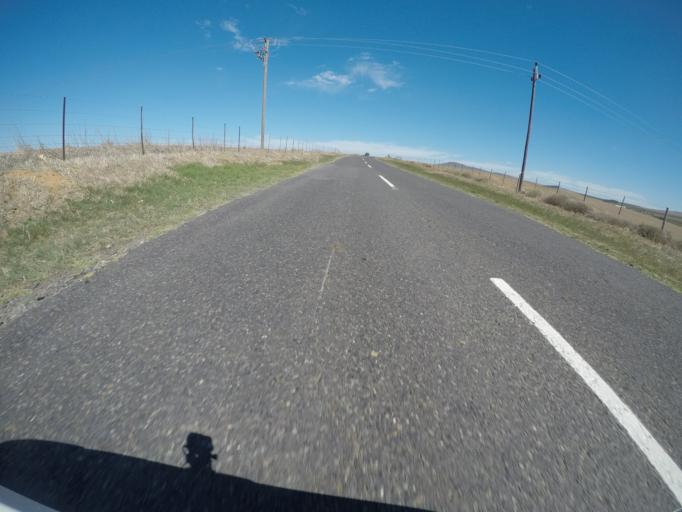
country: ZA
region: Western Cape
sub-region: City of Cape Town
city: Atlantis
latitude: -33.6834
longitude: 18.6010
